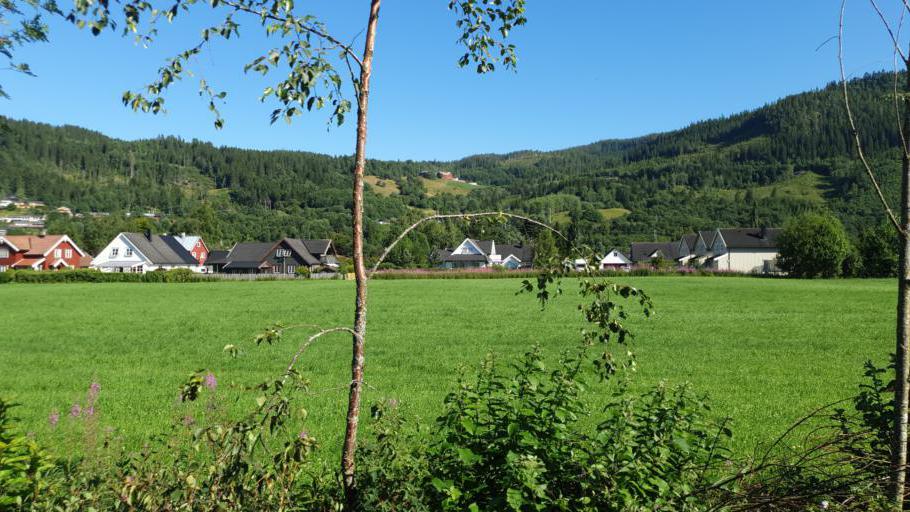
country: NO
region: Sor-Trondelag
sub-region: Orkdal
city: Orkanger
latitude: 63.2865
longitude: 9.8420
